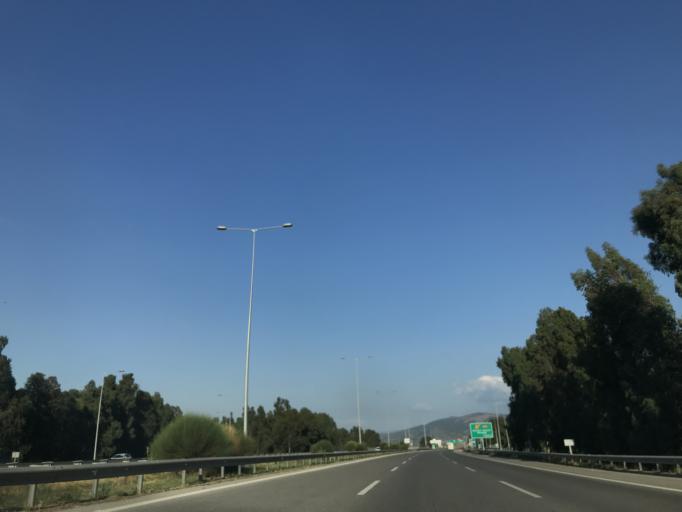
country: TR
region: Aydin
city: Aydin
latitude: 37.8197
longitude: 27.8438
